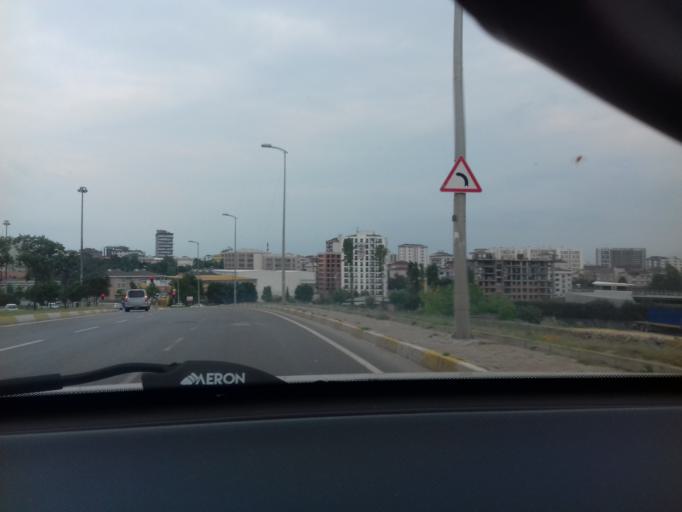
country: TR
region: Istanbul
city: Icmeler
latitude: 40.8767
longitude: 29.3379
